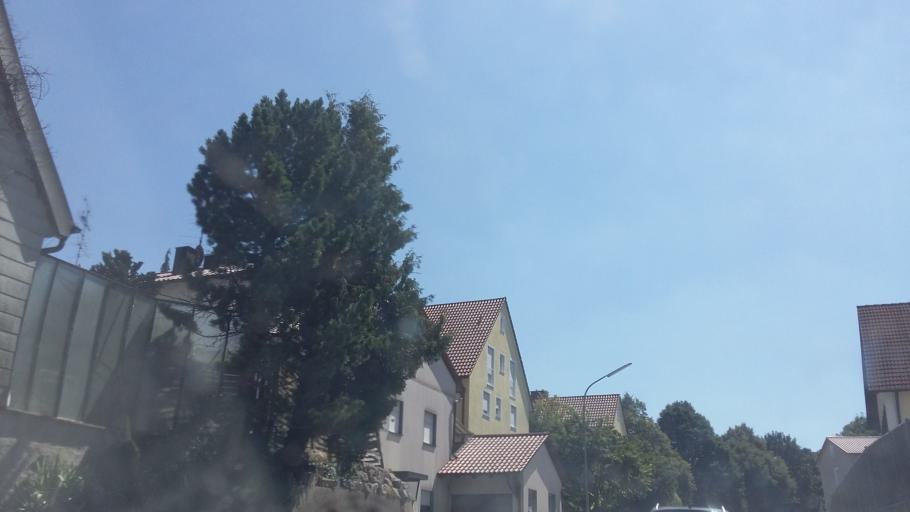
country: DE
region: Bavaria
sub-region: Upper Bavaria
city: Sulzemoos
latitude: 48.2900
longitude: 11.2658
